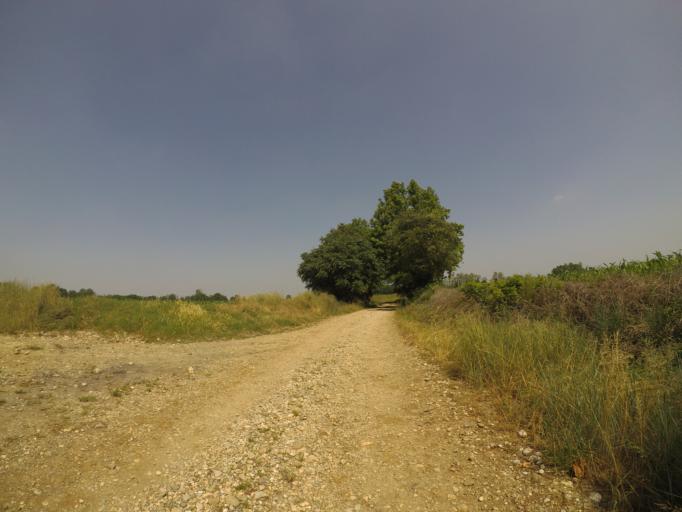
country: IT
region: Friuli Venezia Giulia
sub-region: Provincia di Udine
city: Bertiolo
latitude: 45.9624
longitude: 13.0866
